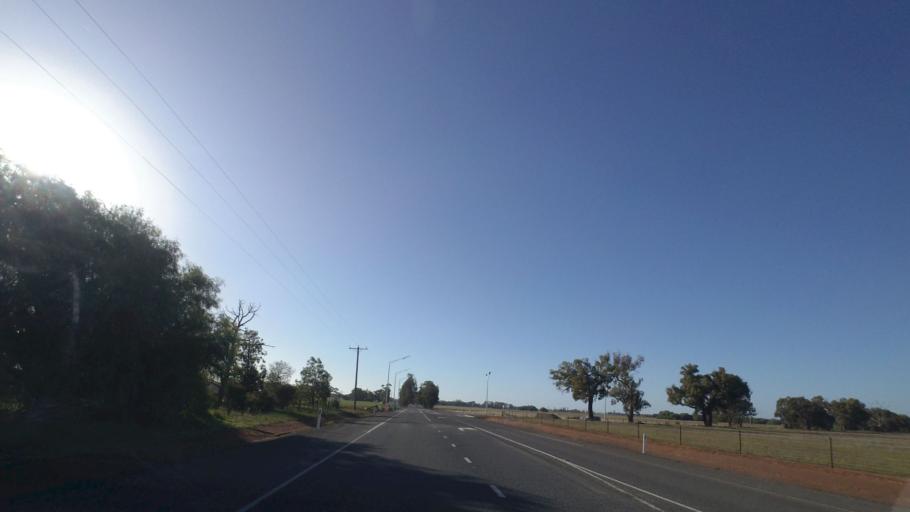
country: AU
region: Victoria
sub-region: Greater Bendigo
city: Epsom
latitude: -36.6510
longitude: 144.5227
